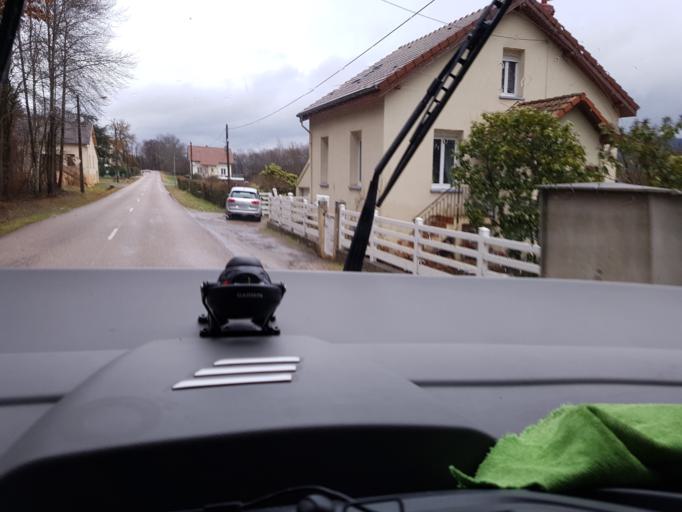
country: FR
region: Lorraine
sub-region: Departement des Vosges
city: Saint-Michel-sur-Meurthe
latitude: 48.2992
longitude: 6.9162
